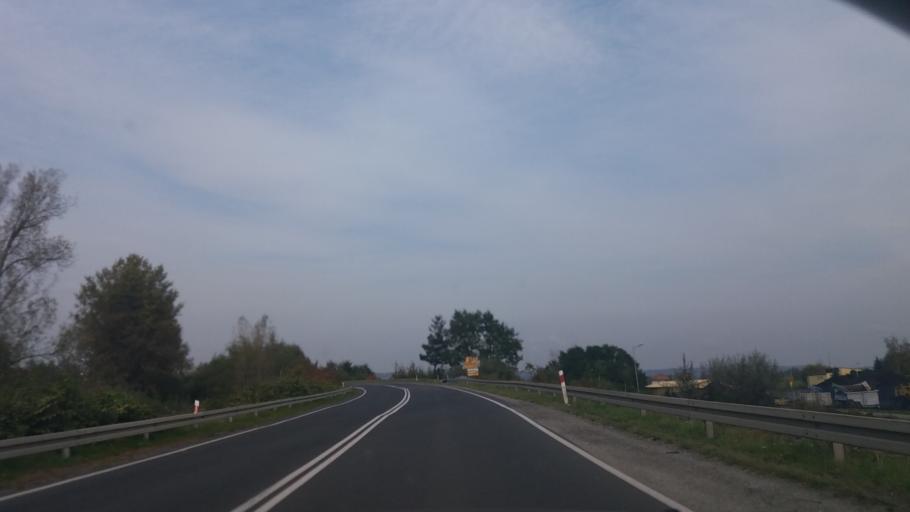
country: PL
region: Lesser Poland Voivodeship
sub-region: Powiat oswiecimski
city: Zator
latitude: 50.0262
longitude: 19.4364
